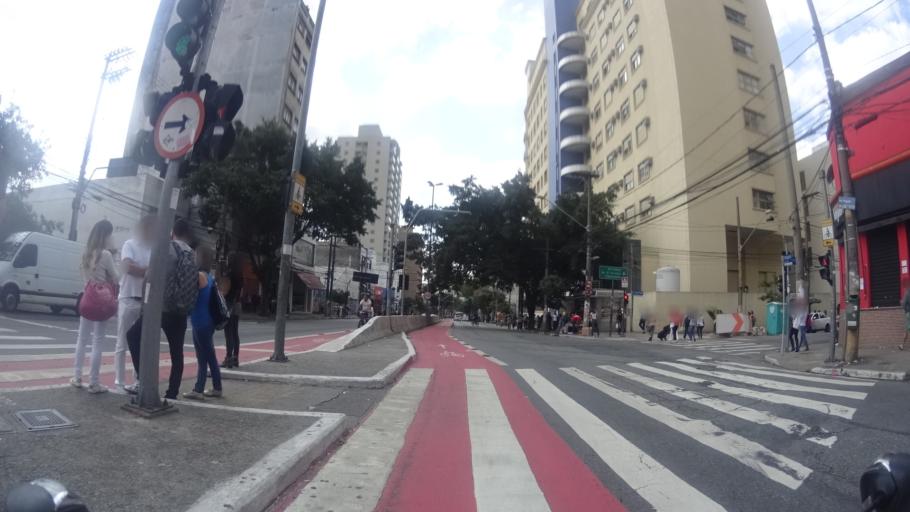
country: BR
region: Sao Paulo
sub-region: Sao Paulo
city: Sao Paulo
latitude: -23.5630
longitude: -46.6388
